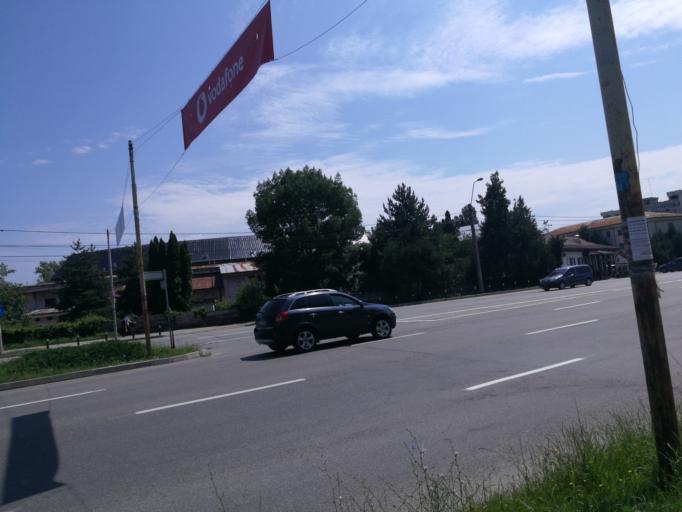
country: RO
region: Arges
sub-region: Comuna Bradu
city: Geamana
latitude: 44.8406
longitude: 24.8959
